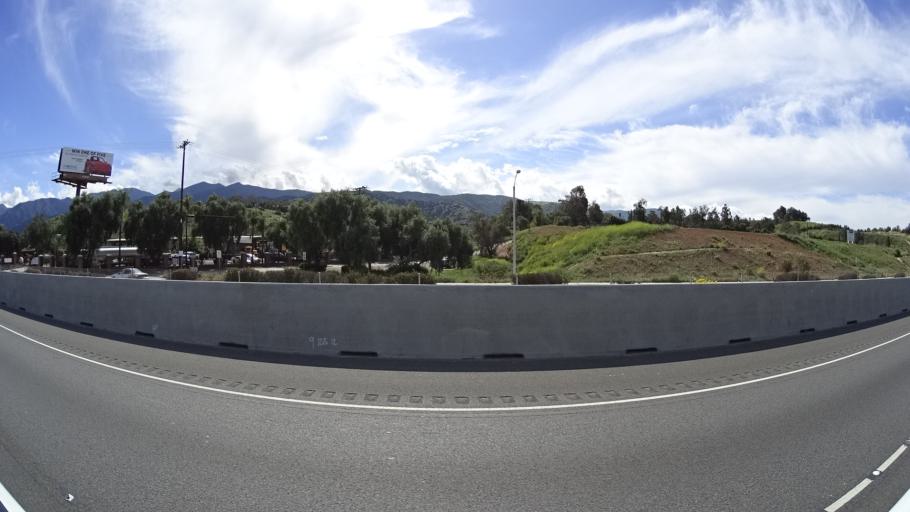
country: US
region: California
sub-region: Riverside County
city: El Cerrito
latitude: 33.8008
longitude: -117.5042
